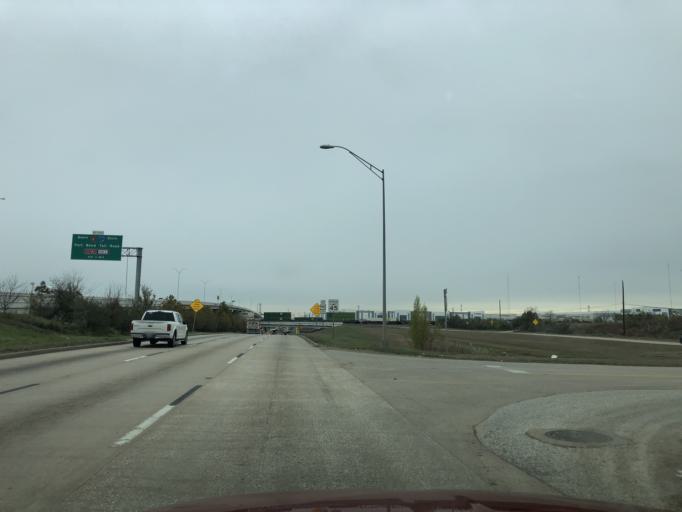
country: US
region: Texas
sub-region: Fort Bend County
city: Missouri City
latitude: 29.6288
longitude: -95.5215
